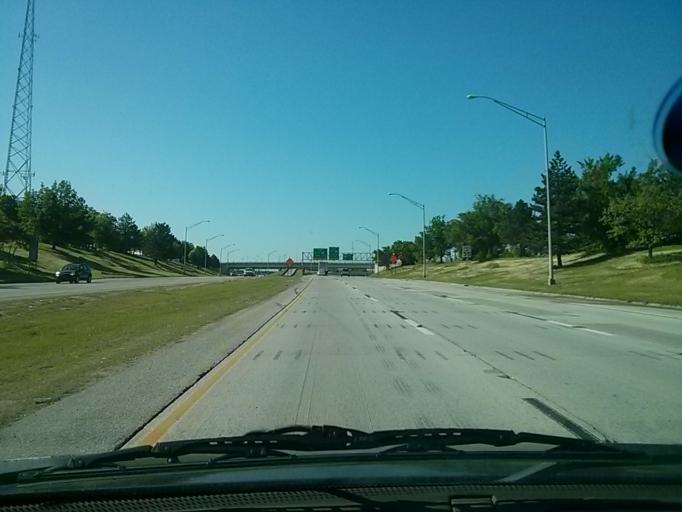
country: US
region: Oklahoma
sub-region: Tulsa County
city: Tulsa
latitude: 36.1656
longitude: -95.9806
